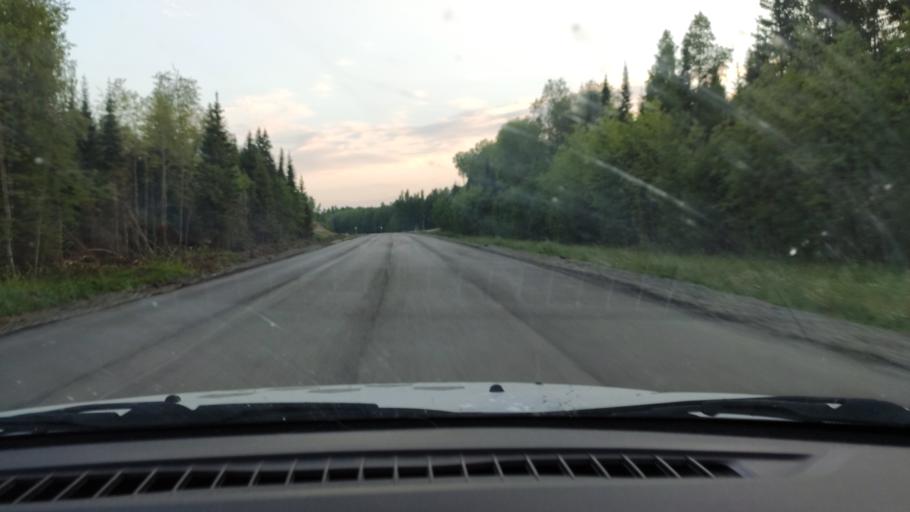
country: RU
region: Perm
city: Siva
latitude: 58.4774
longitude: 54.4019
